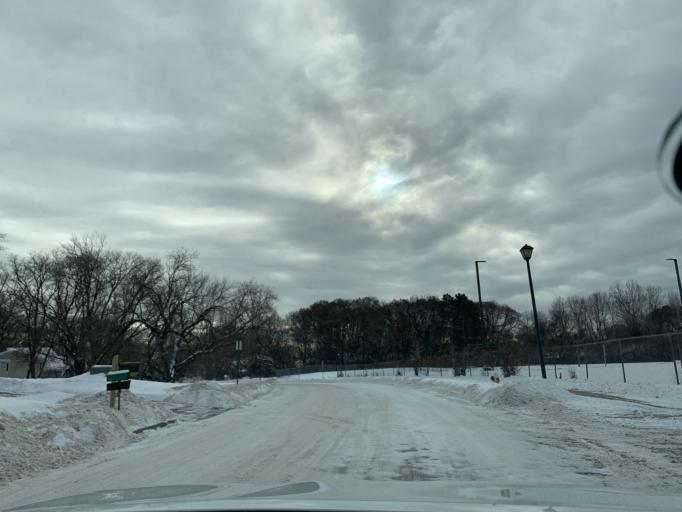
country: US
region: Minnesota
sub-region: Hennepin County
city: West Coon Rapids
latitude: 45.1710
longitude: -93.3003
